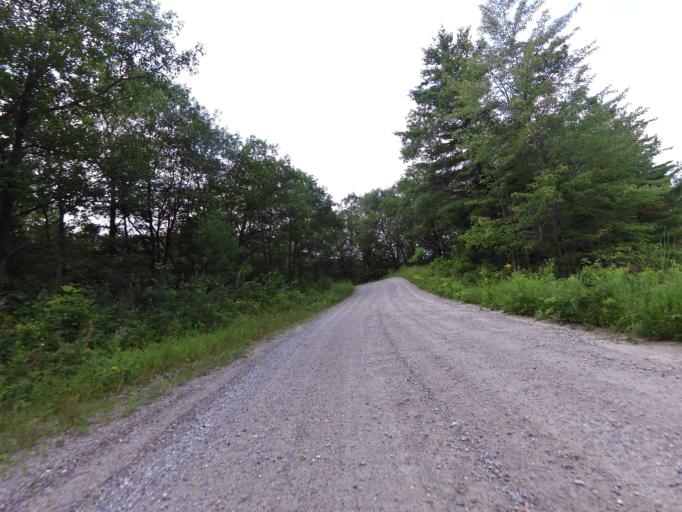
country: CA
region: Ontario
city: Perth
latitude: 44.7699
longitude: -76.6132
